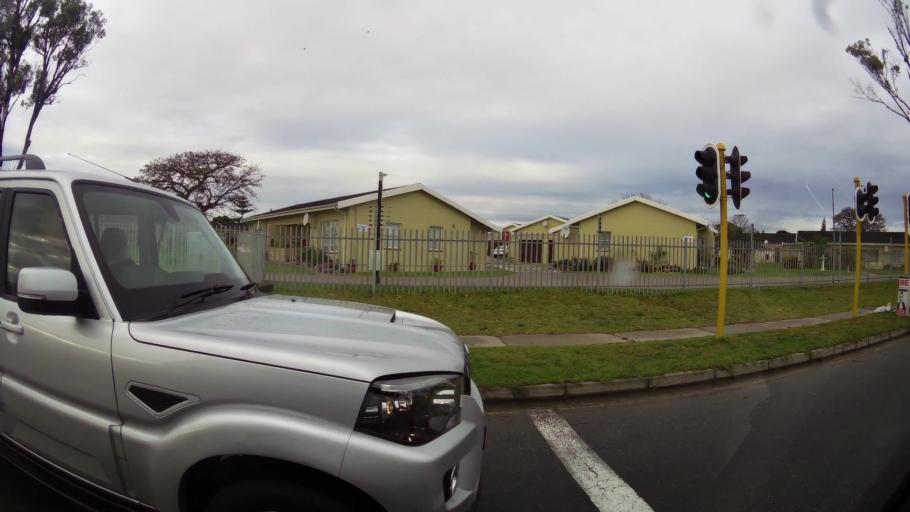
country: ZA
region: Eastern Cape
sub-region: Nelson Mandela Bay Metropolitan Municipality
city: Port Elizabeth
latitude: -33.9818
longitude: 25.5606
